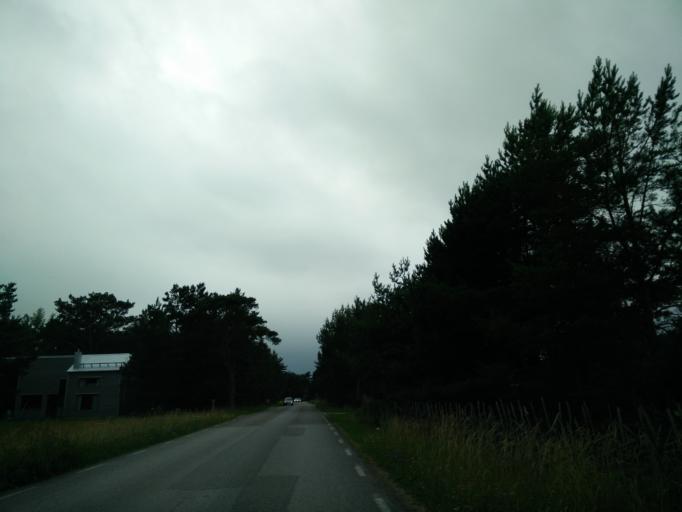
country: SE
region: Gotland
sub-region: Gotland
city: Slite
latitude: 57.9713
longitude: 19.2374
